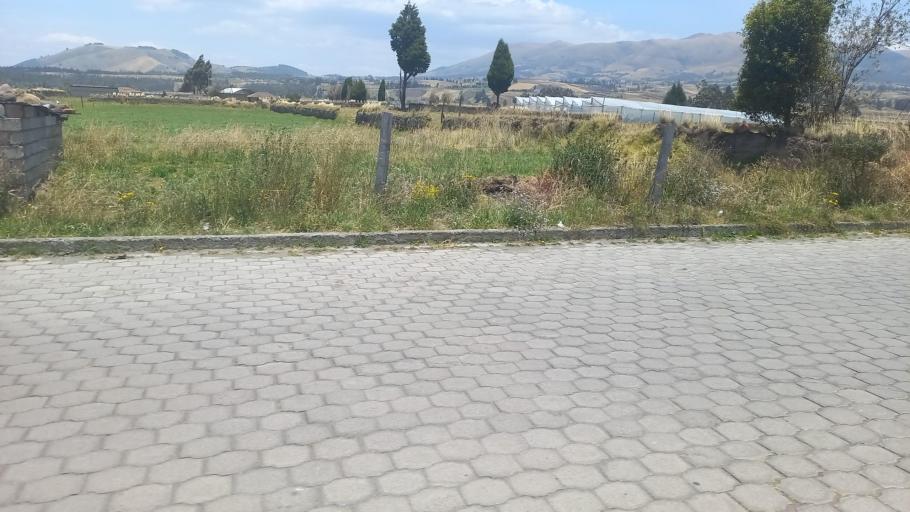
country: EC
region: Pichincha
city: Cayambe
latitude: 0.1420
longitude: -78.0697
